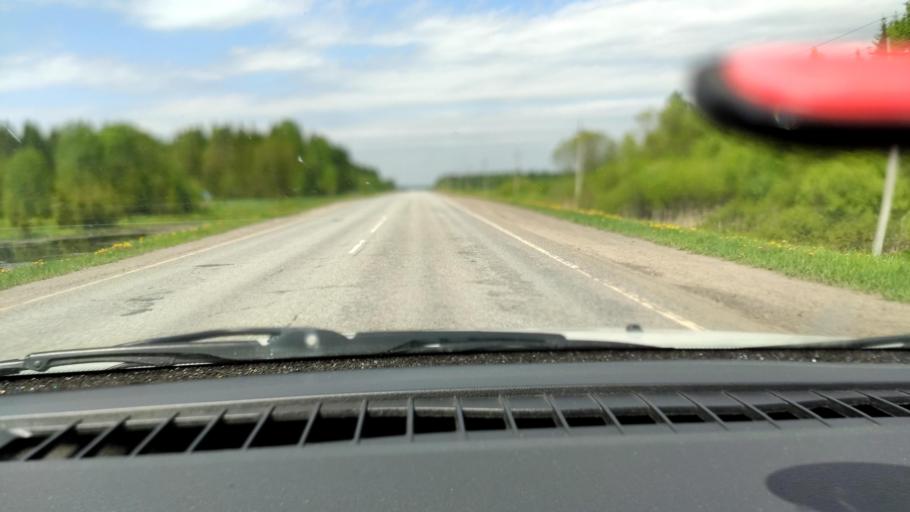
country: RU
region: Perm
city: Bershet'
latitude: 57.7637
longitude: 56.3585
